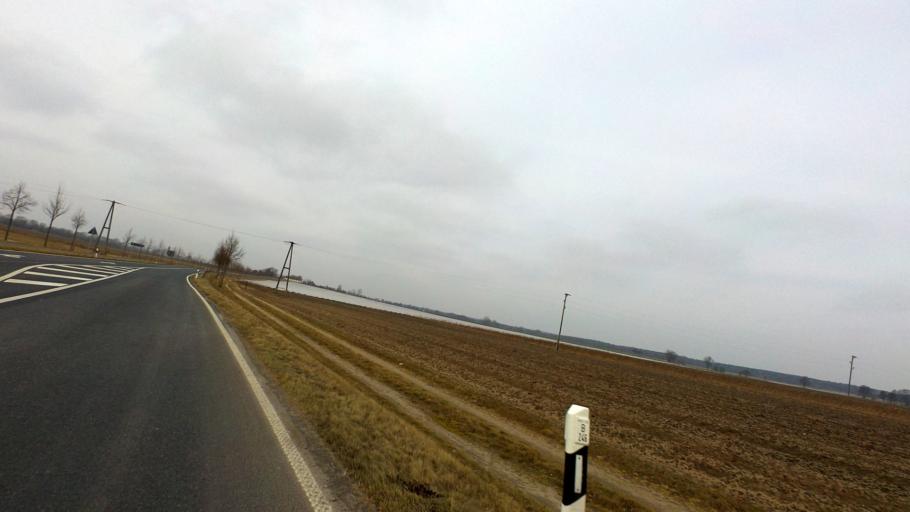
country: DE
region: Brandenburg
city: Beelitz
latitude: 52.2315
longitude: 13.0080
